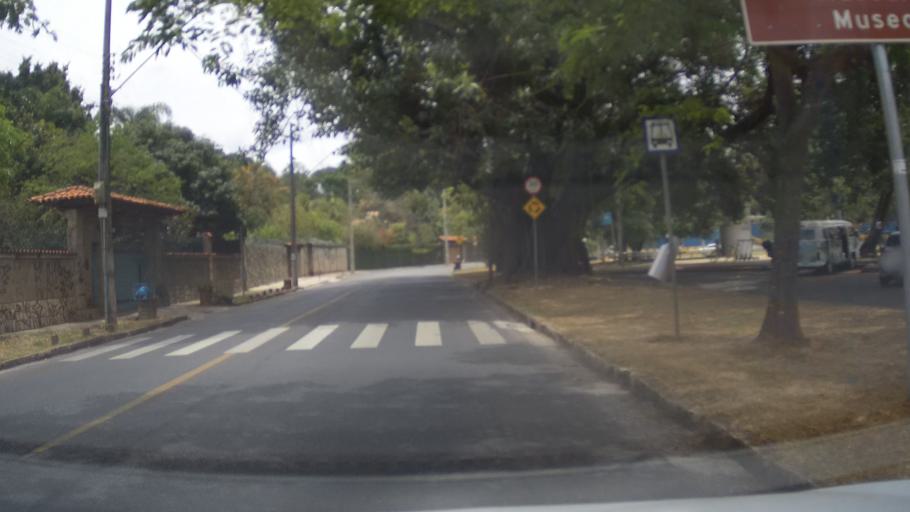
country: BR
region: Minas Gerais
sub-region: Belo Horizonte
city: Belo Horizonte
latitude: -19.8462
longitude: -43.9989
